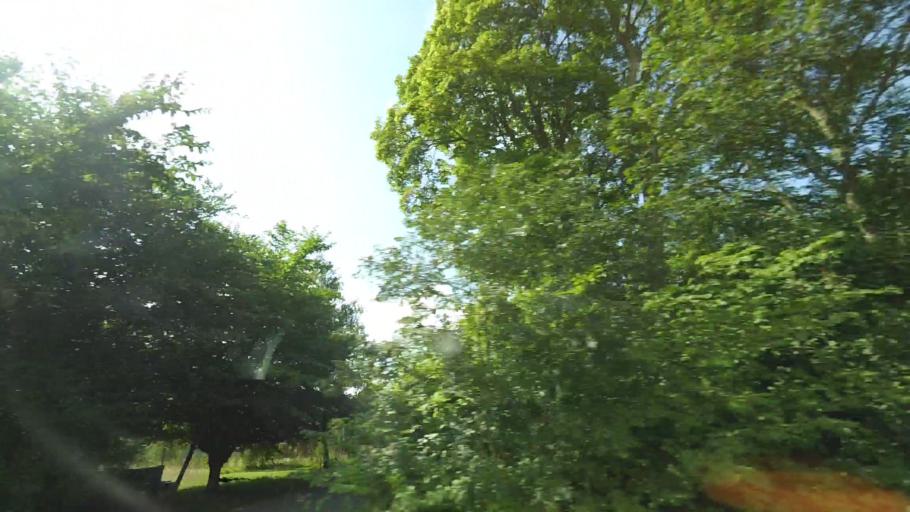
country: DK
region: Central Jutland
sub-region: Syddjurs Kommune
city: Ryomgard
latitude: 56.4662
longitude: 10.5181
